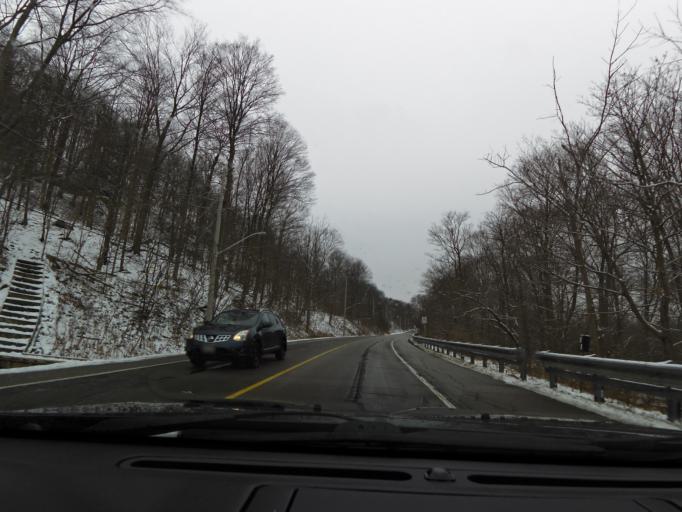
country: CA
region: Ontario
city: Ancaster
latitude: 43.2414
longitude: -79.9573
